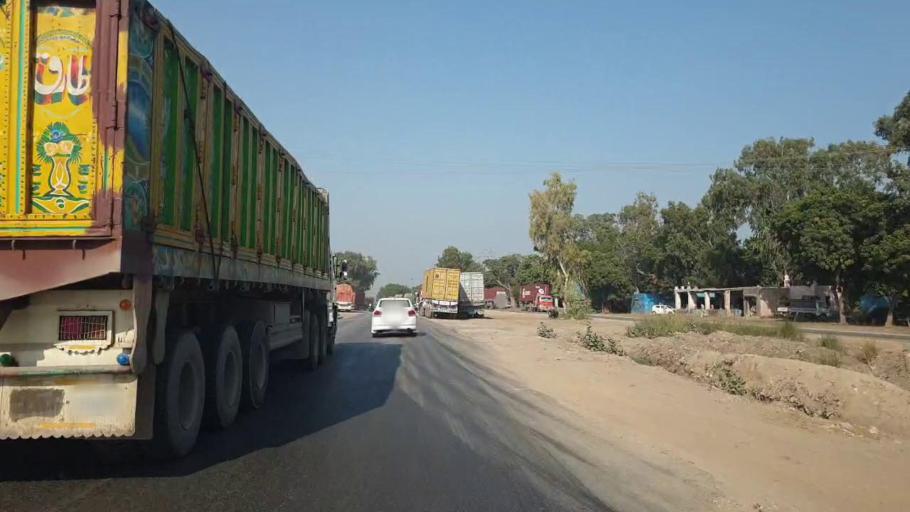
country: PK
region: Sindh
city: Matiari
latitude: 25.5129
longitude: 68.4288
